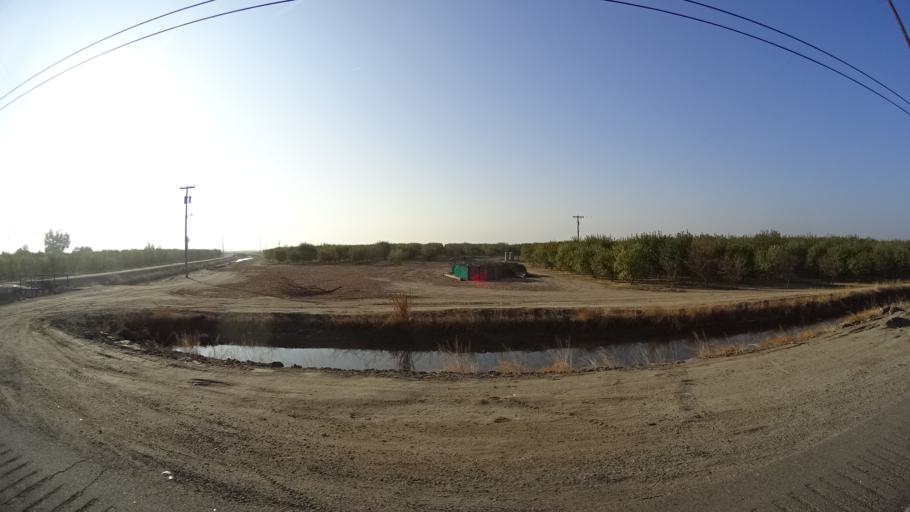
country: US
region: California
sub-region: Kern County
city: Greenfield
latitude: 35.2668
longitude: -118.9871
